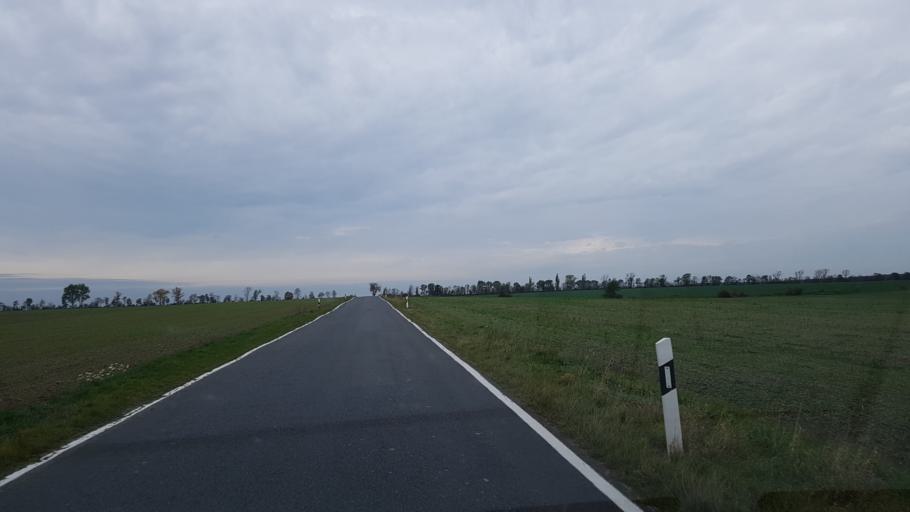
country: DE
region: Saxony
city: Dahlen
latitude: 51.3709
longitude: 12.9792
